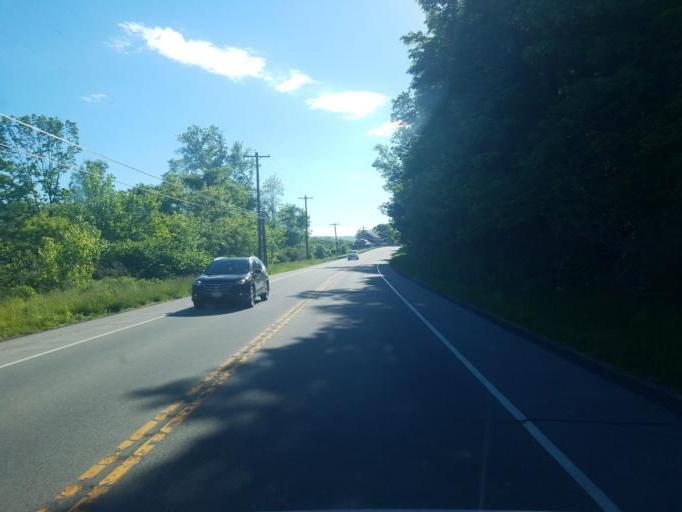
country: US
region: New York
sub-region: Herkimer County
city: Little Falls
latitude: 43.0230
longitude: -74.8965
